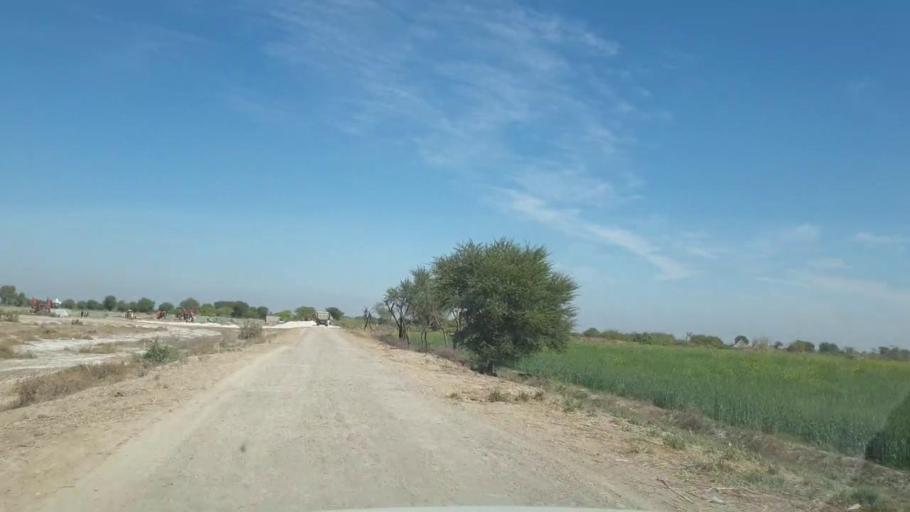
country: PK
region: Sindh
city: Pithoro
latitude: 25.6357
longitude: 69.2226
